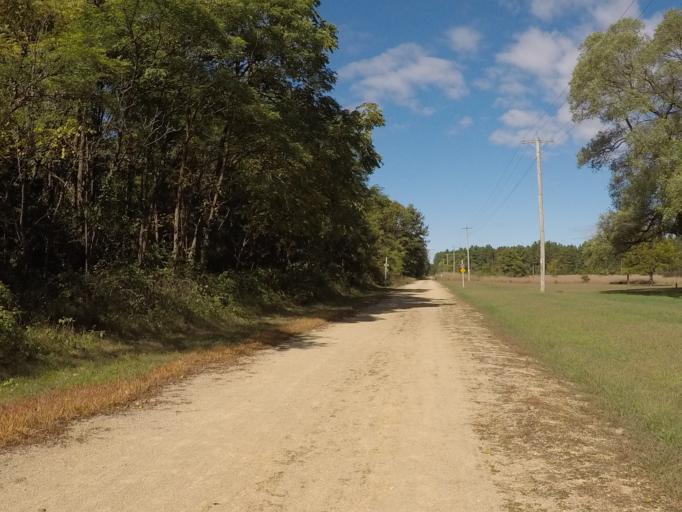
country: US
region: Wisconsin
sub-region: Sauk County
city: Spring Green
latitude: 43.1836
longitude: -90.2076
